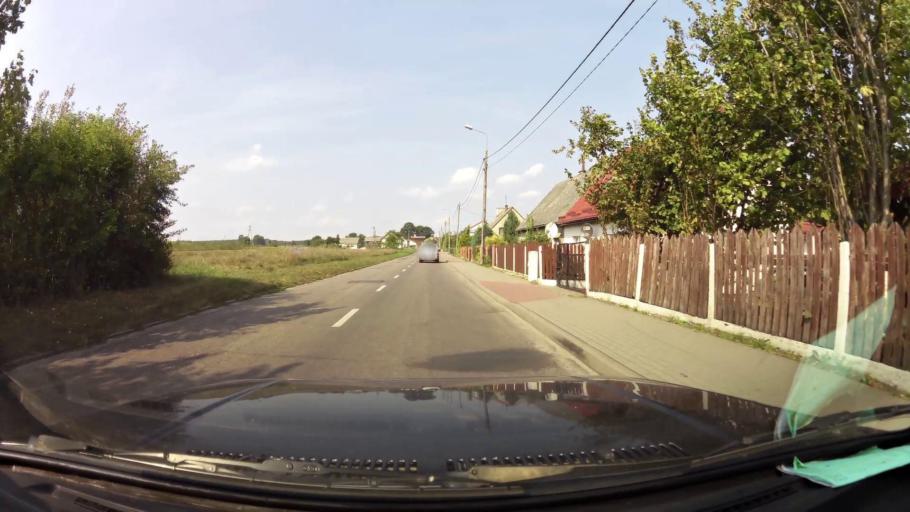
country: PL
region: West Pomeranian Voivodeship
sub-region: Powiat bialogardzki
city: Tychowo
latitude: 54.0701
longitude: 16.2966
